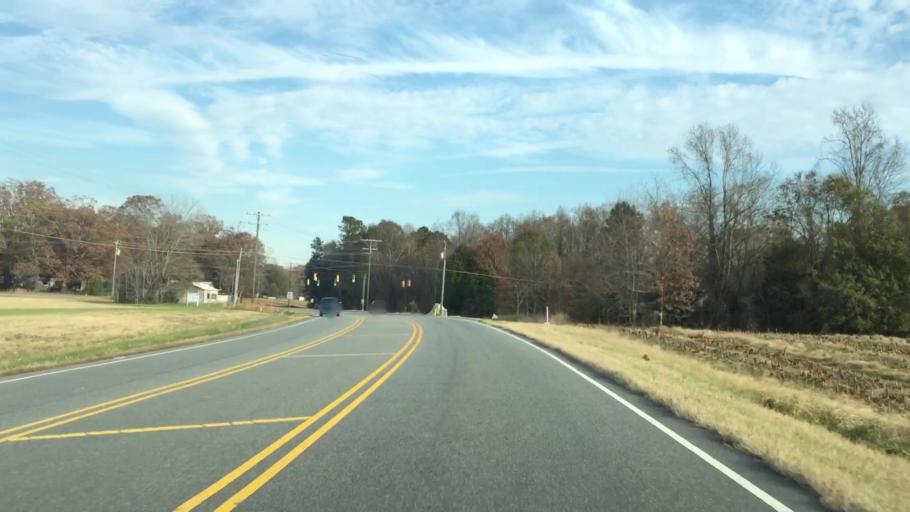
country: US
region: North Carolina
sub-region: Rockingham County
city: Wentworth
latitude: 36.2737
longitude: -79.7910
